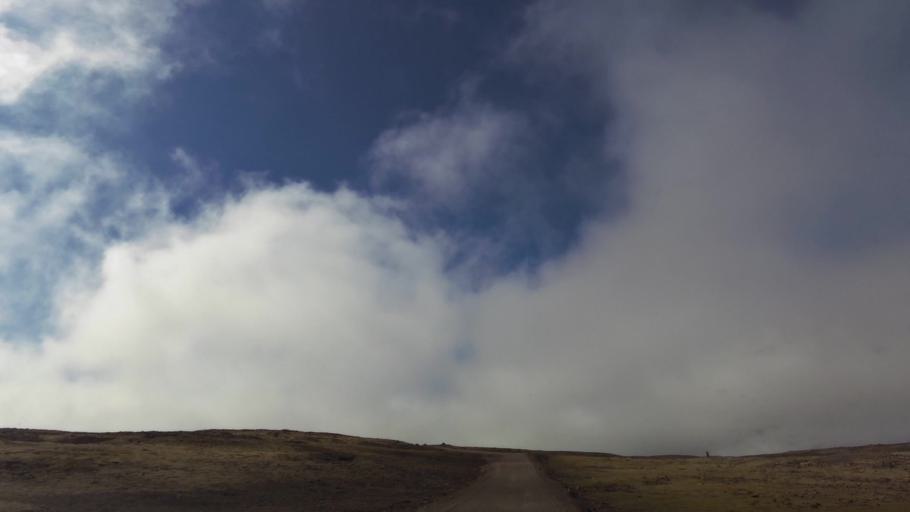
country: IS
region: West
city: Olafsvik
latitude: 65.5565
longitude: -24.2336
